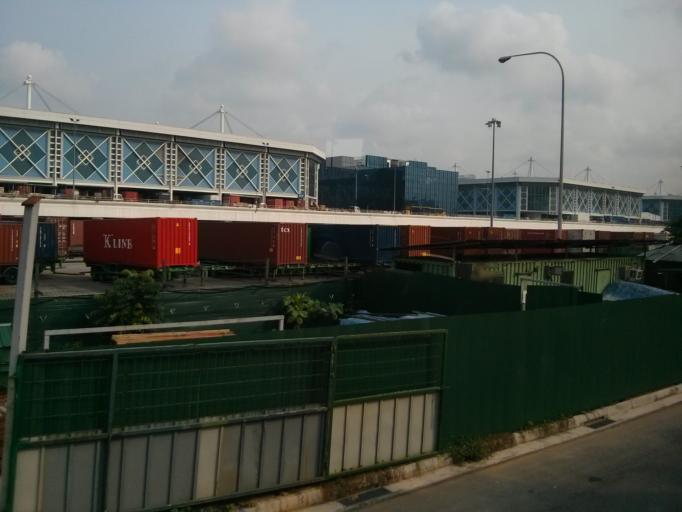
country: SG
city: Singapore
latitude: 1.2692
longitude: 103.8284
